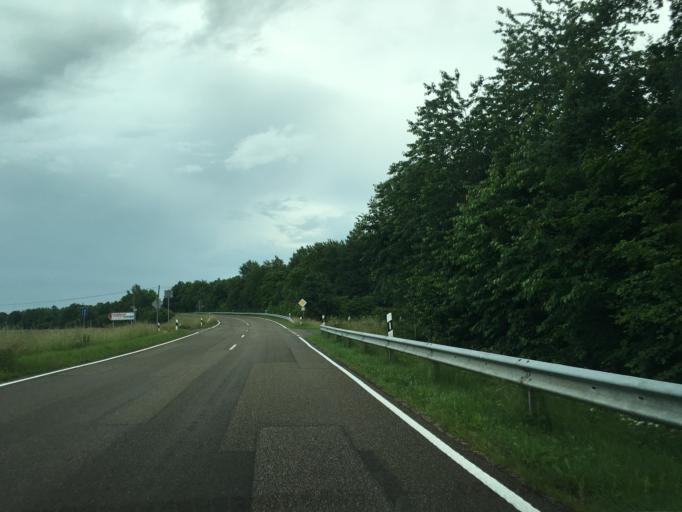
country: DE
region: North Rhine-Westphalia
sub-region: Regierungsbezirk Munster
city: Altenberge
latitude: 52.0126
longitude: 7.4973
